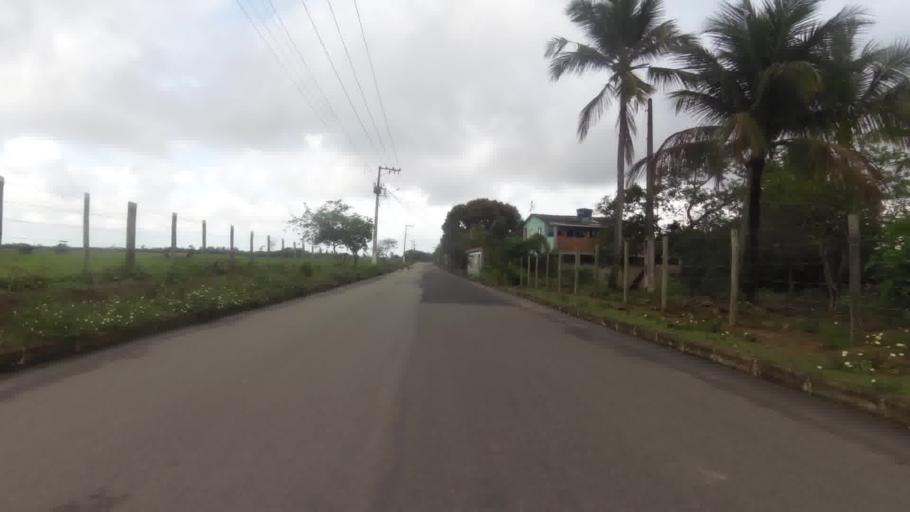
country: BR
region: Espirito Santo
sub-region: Piuma
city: Piuma
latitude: -20.7703
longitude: -40.6299
